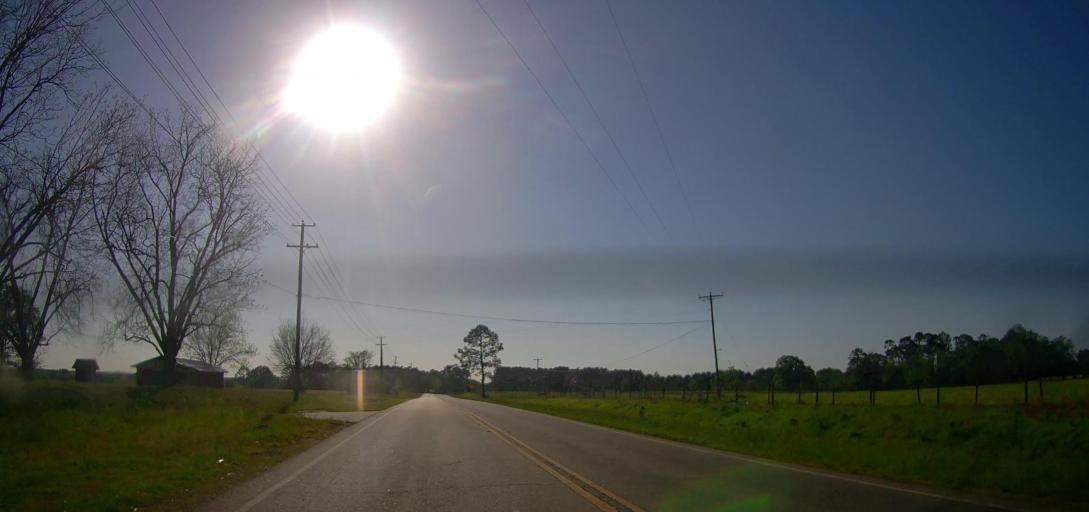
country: US
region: Georgia
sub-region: Ben Hill County
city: Fitzgerald
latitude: 31.6930
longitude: -83.2843
